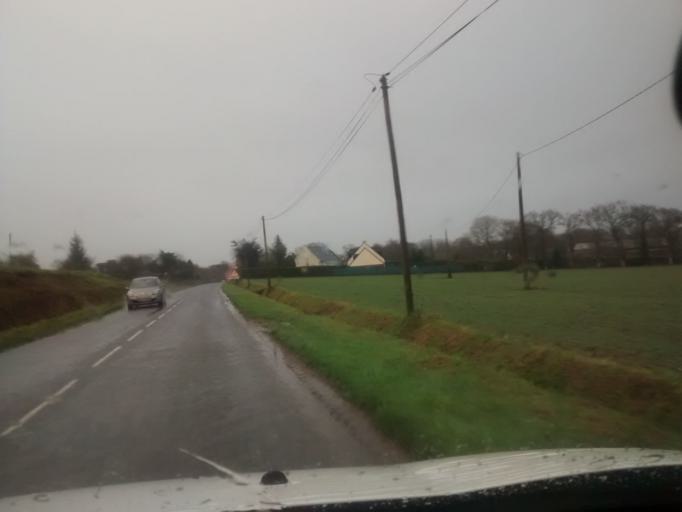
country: FR
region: Brittany
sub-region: Departement d'Ille-et-Vilaine
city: Saint-Pere
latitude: 48.5701
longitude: -1.9078
